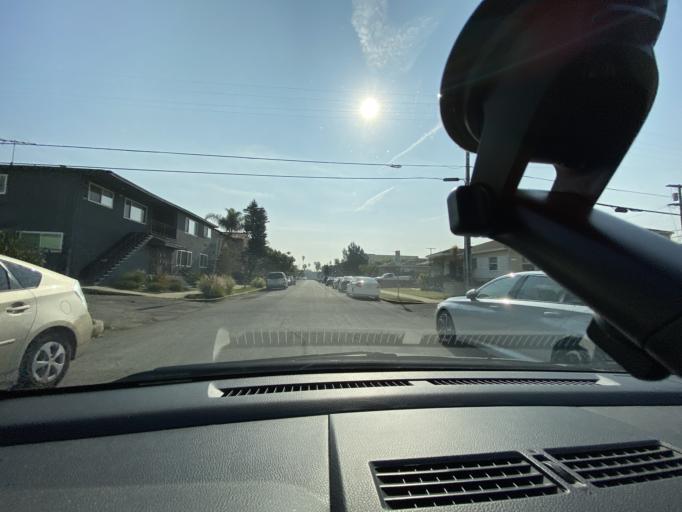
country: US
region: California
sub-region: Los Angeles County
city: Culver City
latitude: 34.0166
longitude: -118.4092
